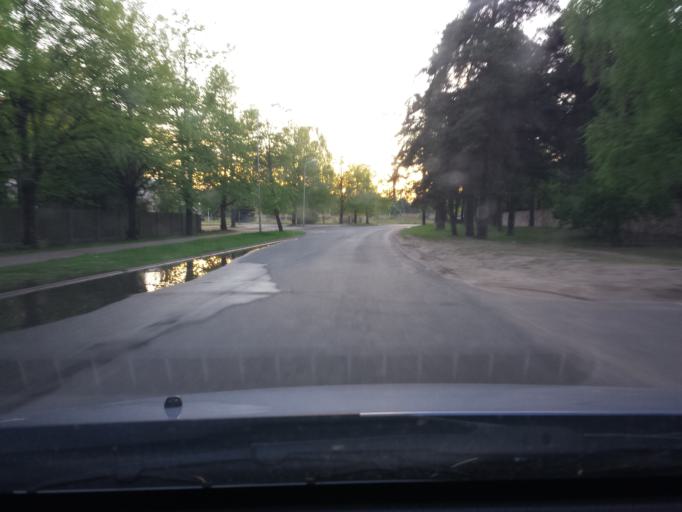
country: LV
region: Riga
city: Riga
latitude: 56.9867
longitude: 24.1434
